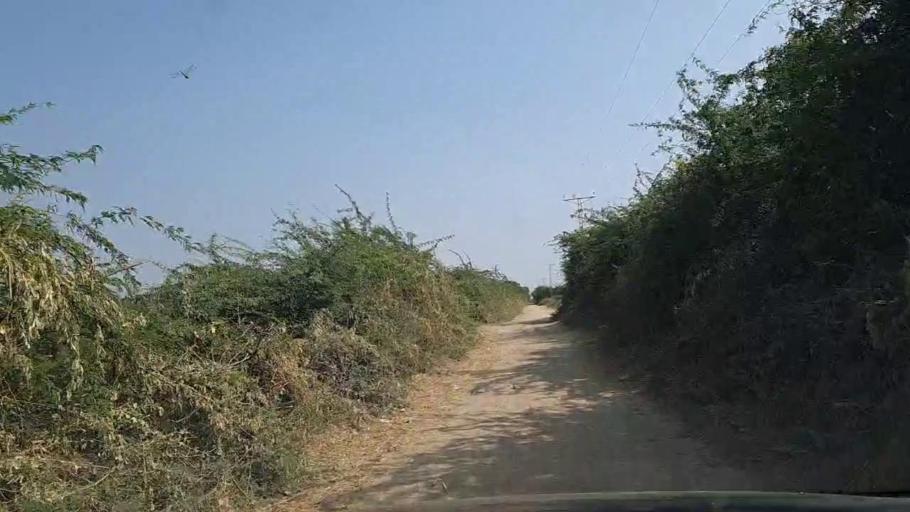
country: PK
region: Sindh
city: Gharo
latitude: 24.7404
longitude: 67.6761
